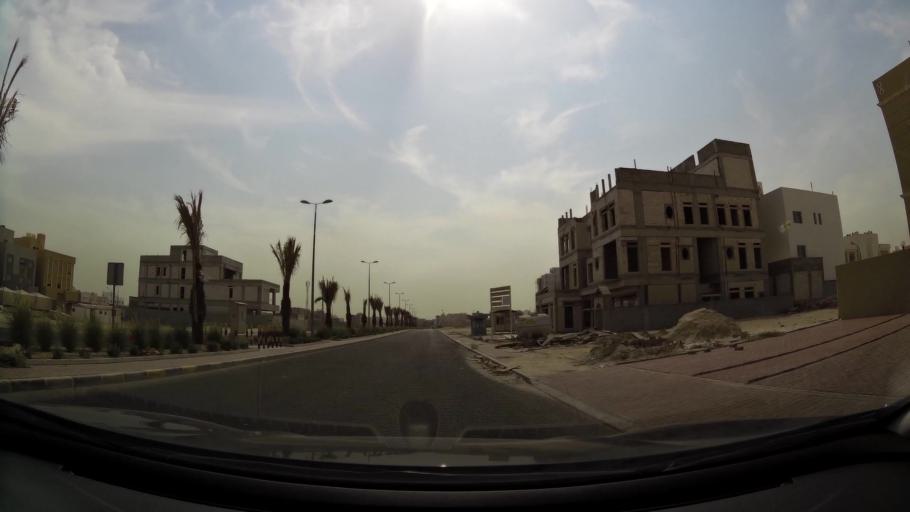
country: KW
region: Al Farwaniyah
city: Janub as Surrah
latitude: 29.2940
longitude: 47.9974
